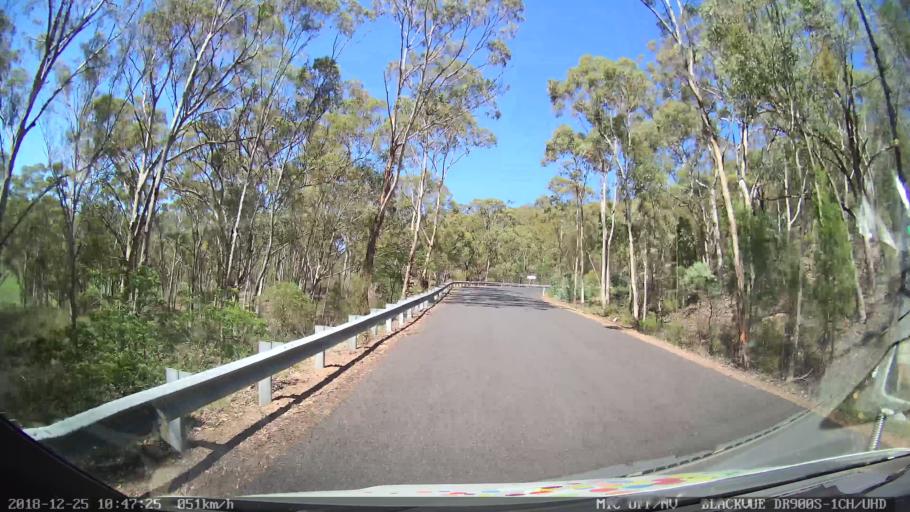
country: AU
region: New South Wales
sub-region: Upper Hunter Shire
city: Merriwa
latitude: -32.4479
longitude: 150.2767
